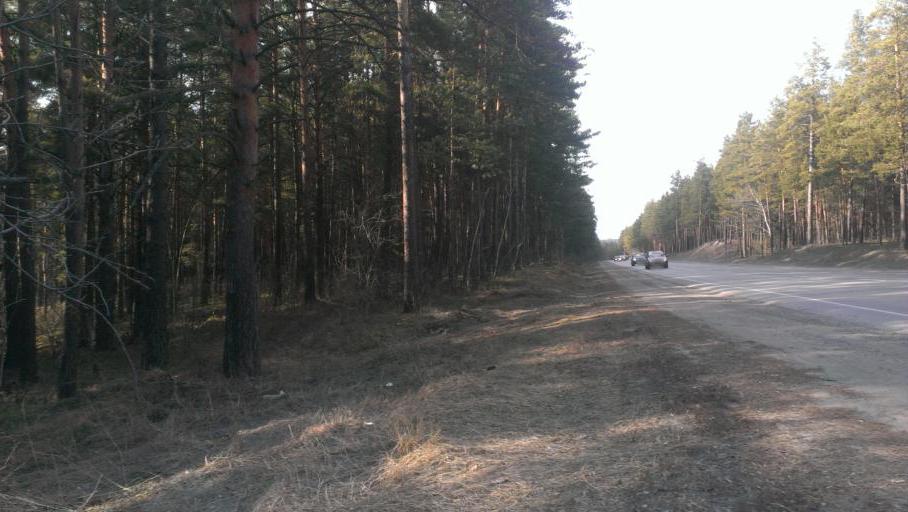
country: RU
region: Altai Krai
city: Yuzhnyy
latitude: 53.2926
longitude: 83.7069
